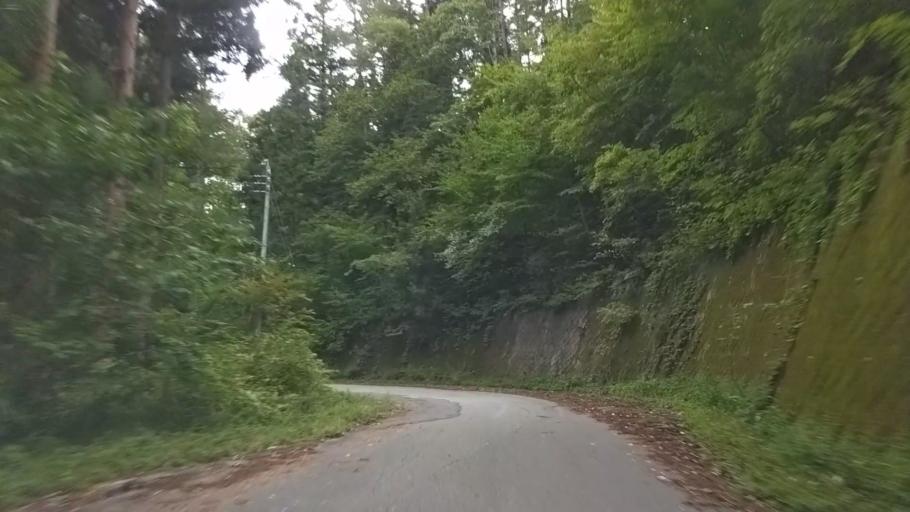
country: JP
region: Nagano
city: Iiyama
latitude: 36.8171
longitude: 138.3780
